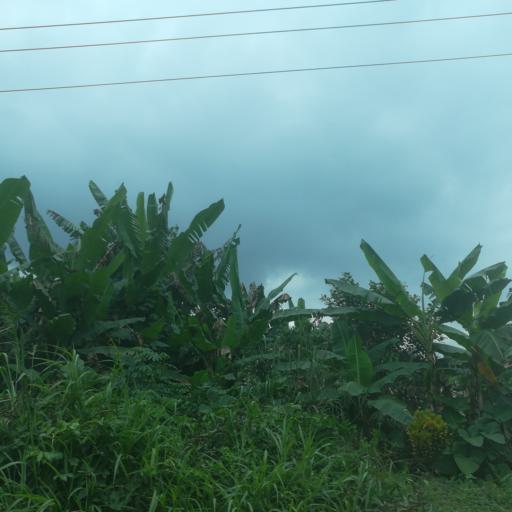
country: NG
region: Lagos
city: Ejirin
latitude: 6.6455
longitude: 3.8450
